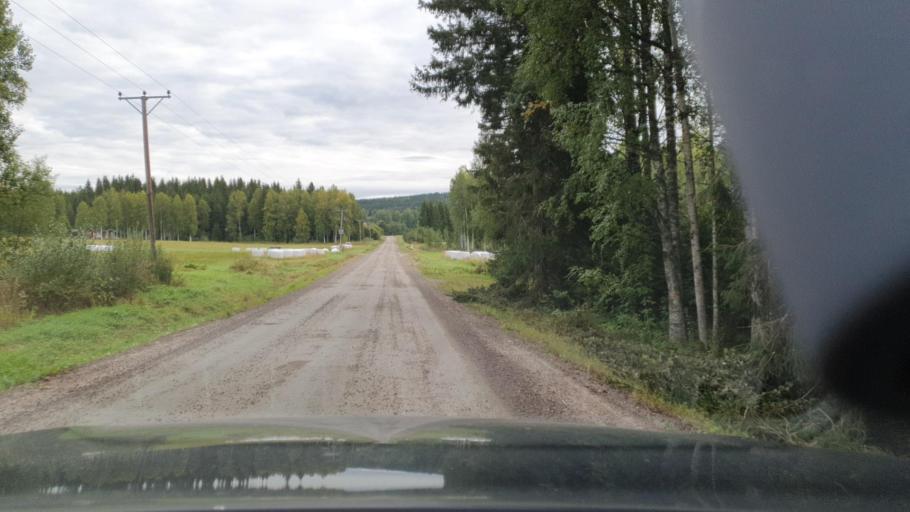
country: SE
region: Vaermland
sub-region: Hagfors Kommun
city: Ekshaerad
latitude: 60.0099
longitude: 13.4593
